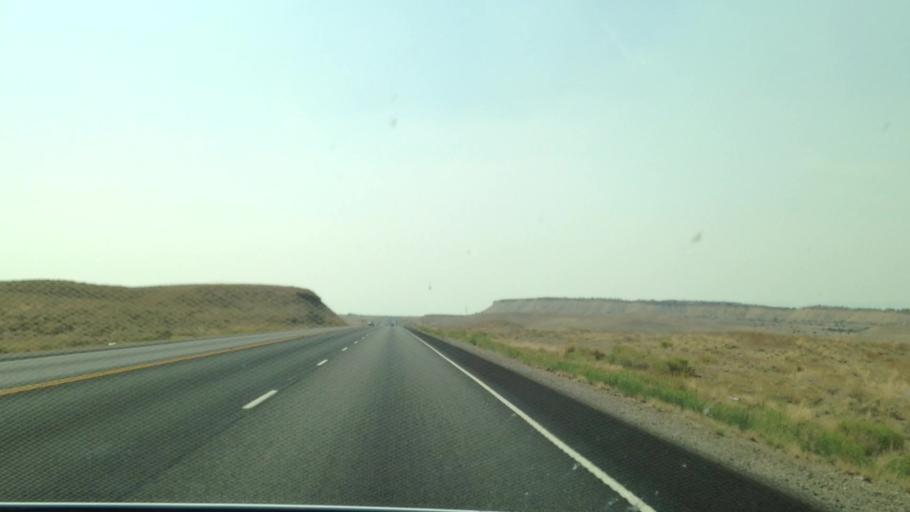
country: US
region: Utah
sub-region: Carbon County
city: Wellington
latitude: 39.5373
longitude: -110.6022
